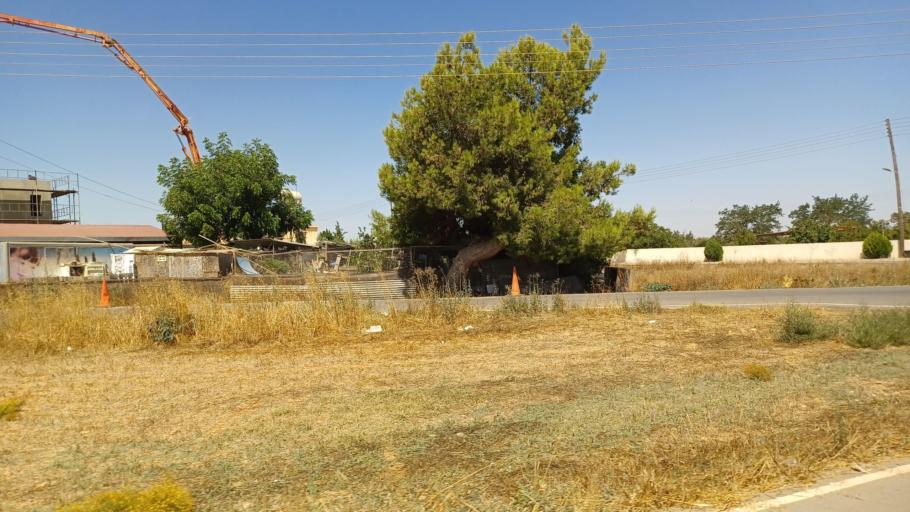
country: CY
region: Ammochostos
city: Avgorou
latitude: 35.0427
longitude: 33.8368
